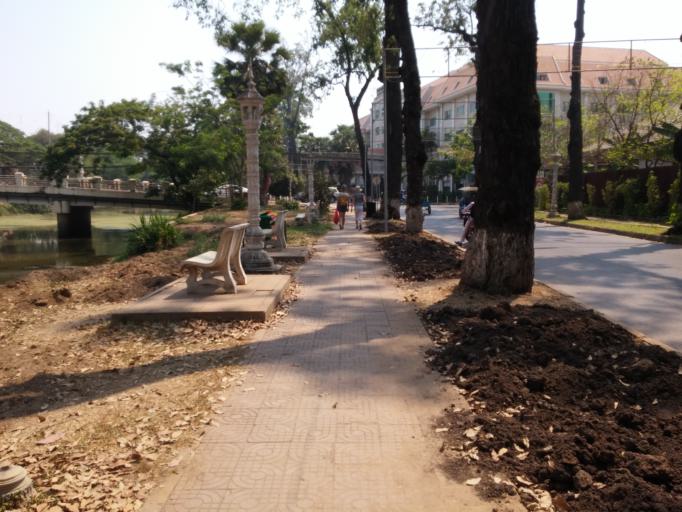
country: KH
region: Siem Reap
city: Siem Reap
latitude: 13.3580
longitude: 103.8584
